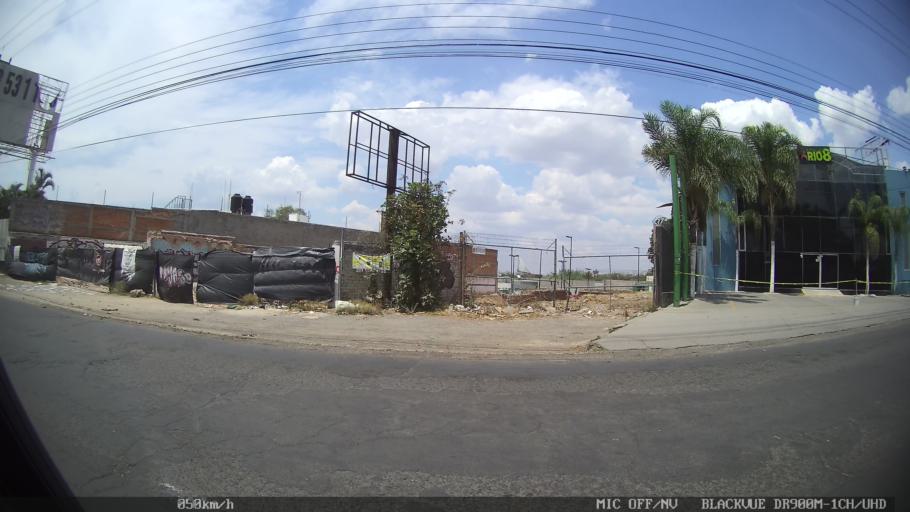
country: MX
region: Jalisco
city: Tlaquepaque
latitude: 20.6380
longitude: -103.2748
